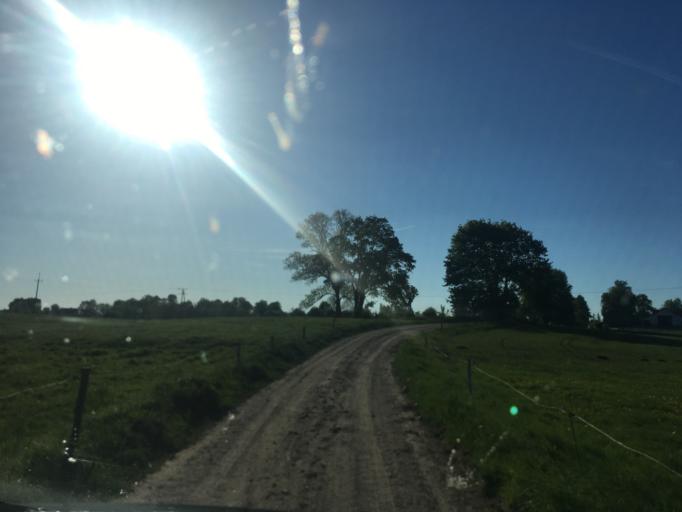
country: PL
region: Warmian-Masurian Voivodeship
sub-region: Powiat piski
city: Ruciane-Nida
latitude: 53.6610
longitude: 21.4798
